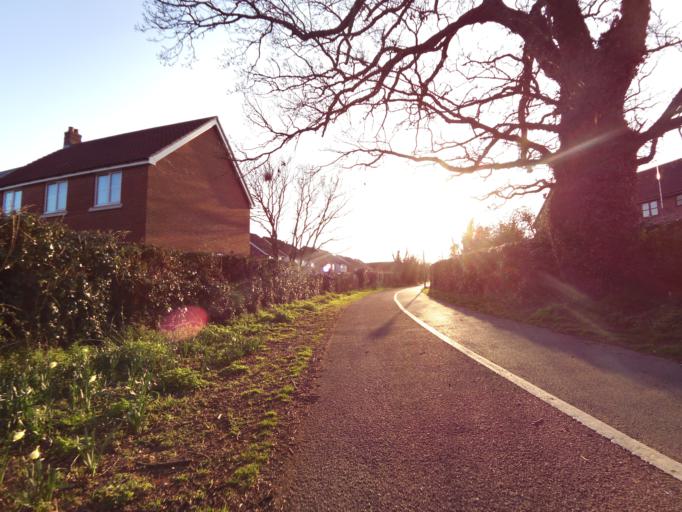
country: GB
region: England
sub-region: Suffolk
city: Kesgrave
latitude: 52.0623
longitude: 1.2488
